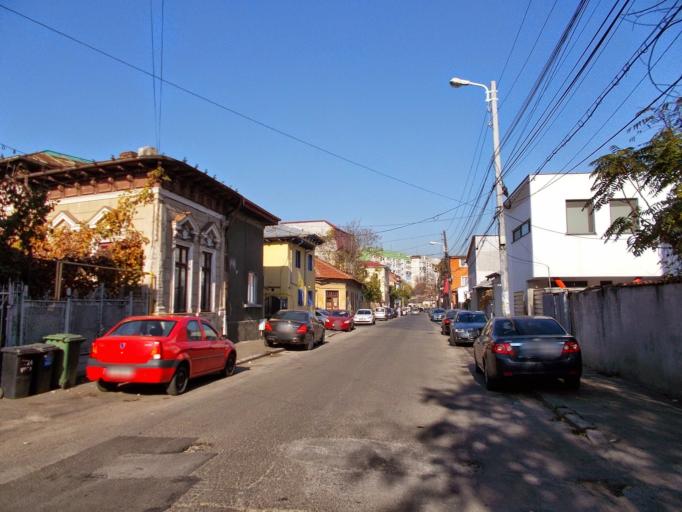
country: RO
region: Bucuresti
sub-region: Municipiul Bucuresti
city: Bucuresti
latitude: 44.4180
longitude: 26.1066
